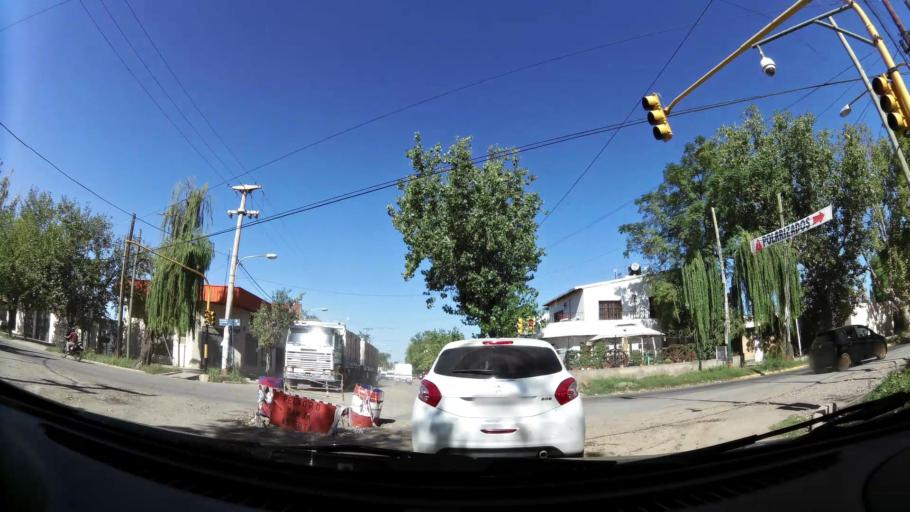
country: AR
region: Mendoza
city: Villa Nueva
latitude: -32.8947
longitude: -68.8018
